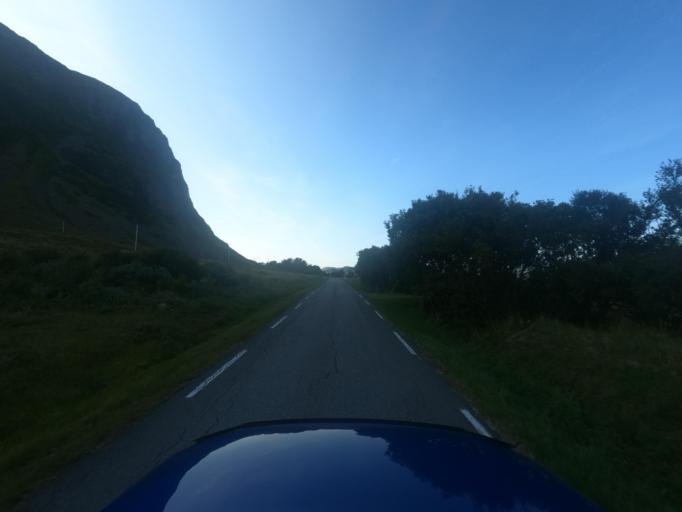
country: NO
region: Nordland
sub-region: Vestvagoy
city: Evjen
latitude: 68.3415
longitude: 13.9278
